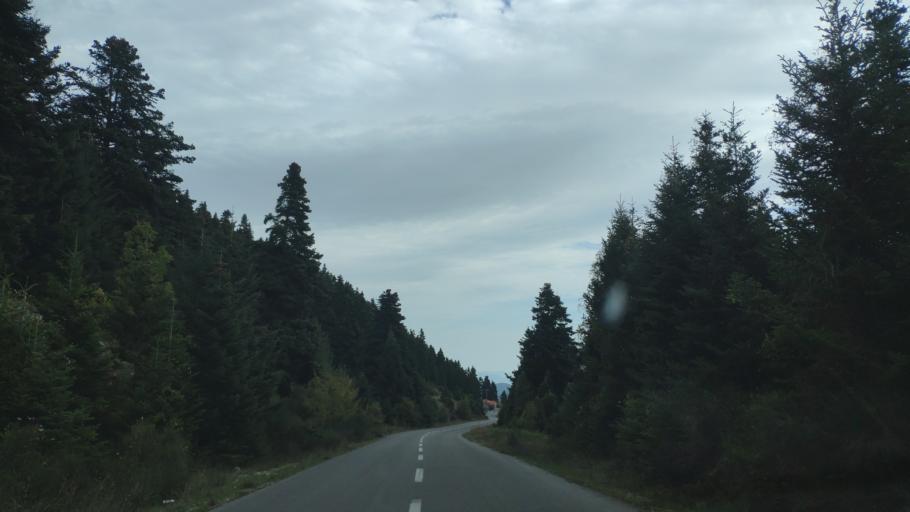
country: GR
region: Central Greece
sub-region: Nomos Fthiotidos
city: Stavros
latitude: 38.7315
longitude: 22.3408
